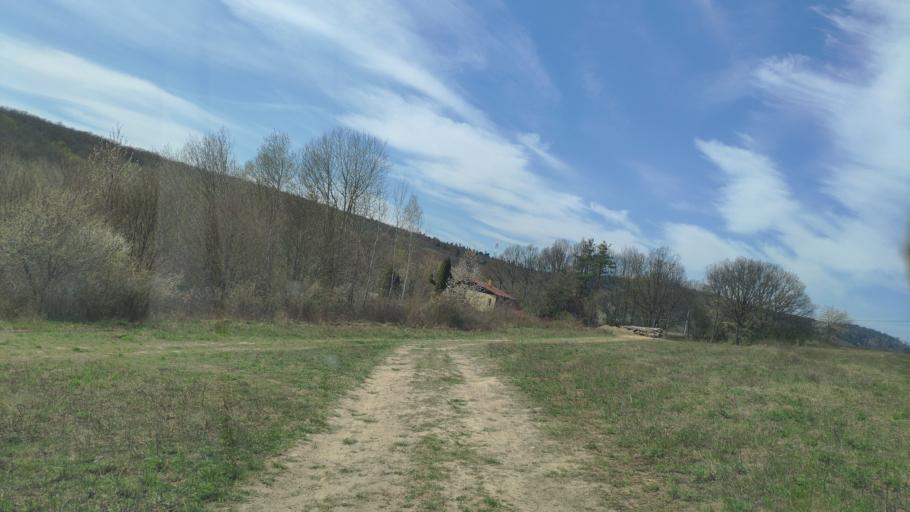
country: SK
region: Kosicky
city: Kosice
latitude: 48.7222
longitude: 21.1944
